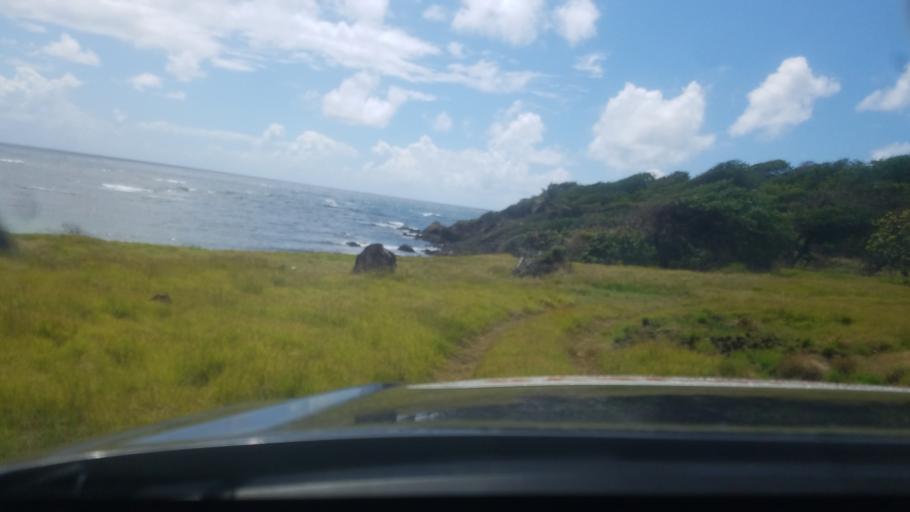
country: LC
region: Praslin
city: Praslin
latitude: 13.8693
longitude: -60.8864
